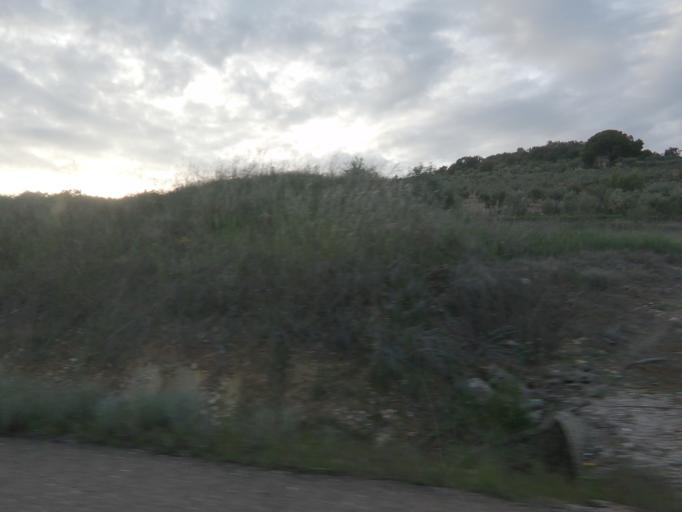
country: ES
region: Extremadura
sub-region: Provincia de Badajoz
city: Puebla de Obando
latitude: 39.1842
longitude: -6.6013
